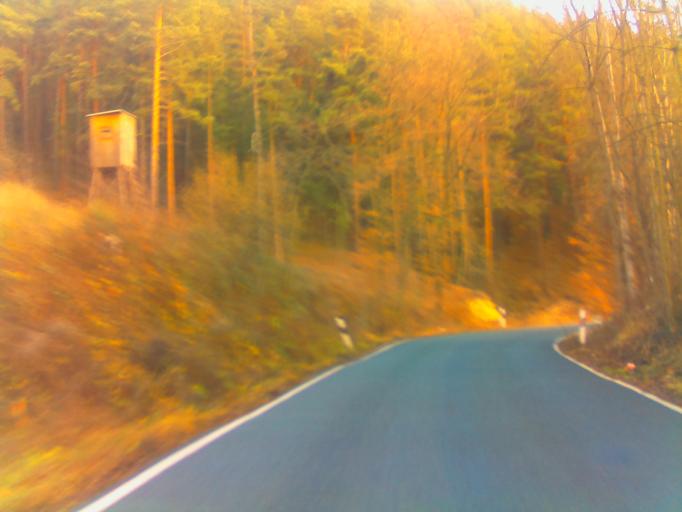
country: DE
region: Thuringia
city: Saalfeld
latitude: 50.6706
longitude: 11.3773
